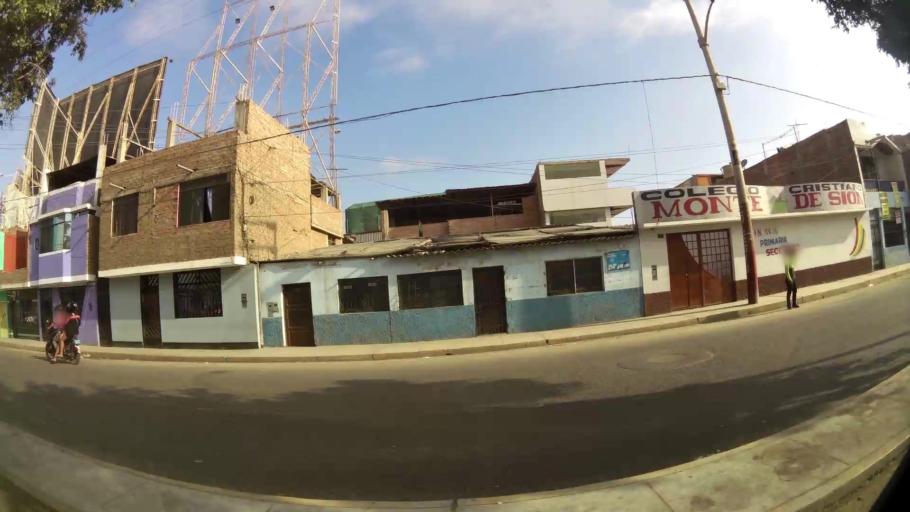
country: PE
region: La Libertad
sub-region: Provincia de Trujillo
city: Trujillo
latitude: -8.1010
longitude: -79.0472
